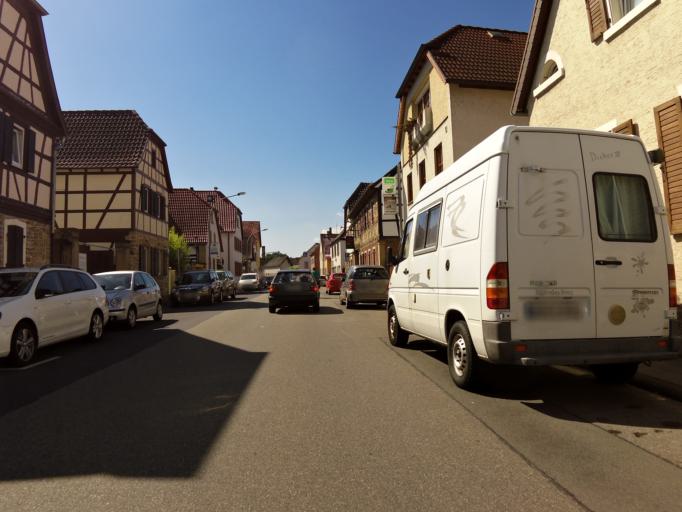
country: DE
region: Rheinland-Pfalz
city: Hassloch
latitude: 49.3607
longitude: 8.2555
